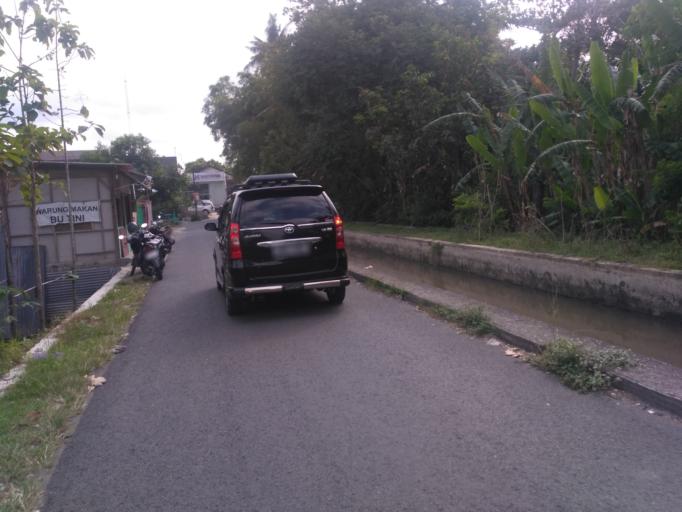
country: ID
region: Daerah Istimewa Yogyakarta
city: Yogyakarta
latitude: -7.7595
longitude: 110.3686
